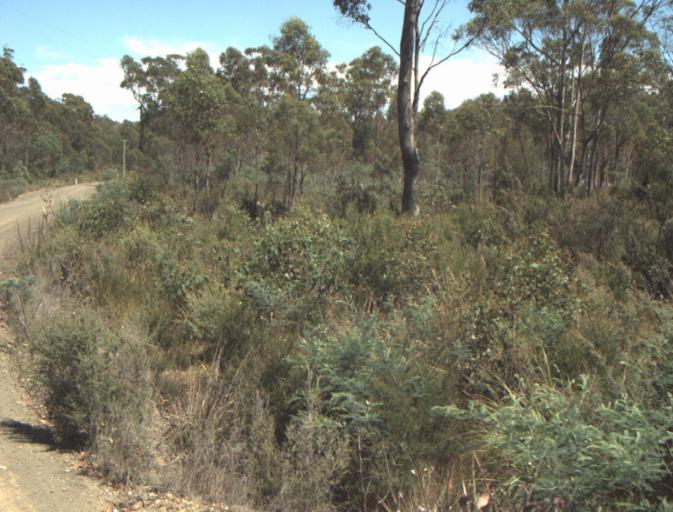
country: AU
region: Tasmania
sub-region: Launceston
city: Mayfield
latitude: -41.2775
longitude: 147.0984
